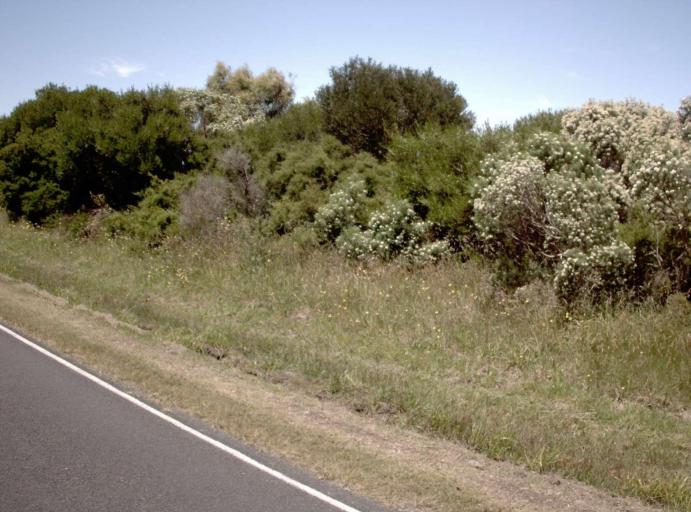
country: AU
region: Victoria
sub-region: Latrobe
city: Morwell
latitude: -38.7847
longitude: 146.1677
